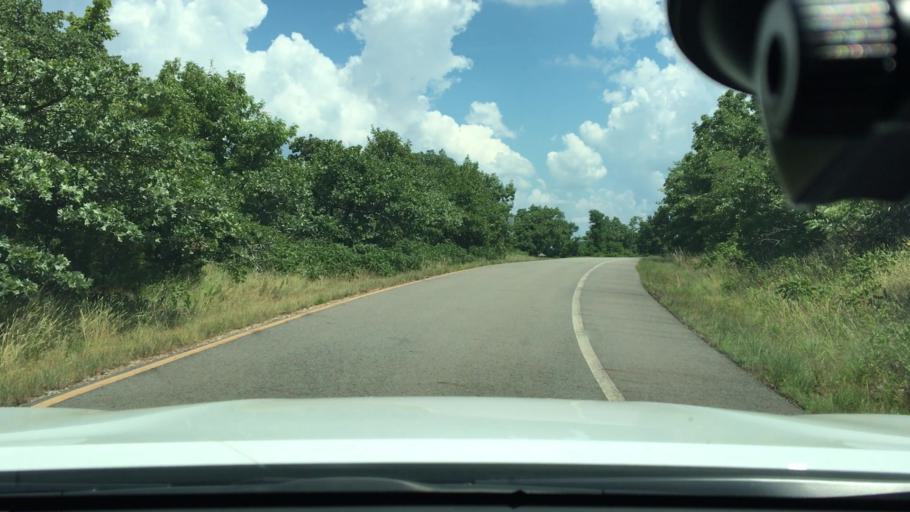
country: US
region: Arkansas
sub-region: Logan County
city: Paris
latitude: 35.1748
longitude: -93.6464
